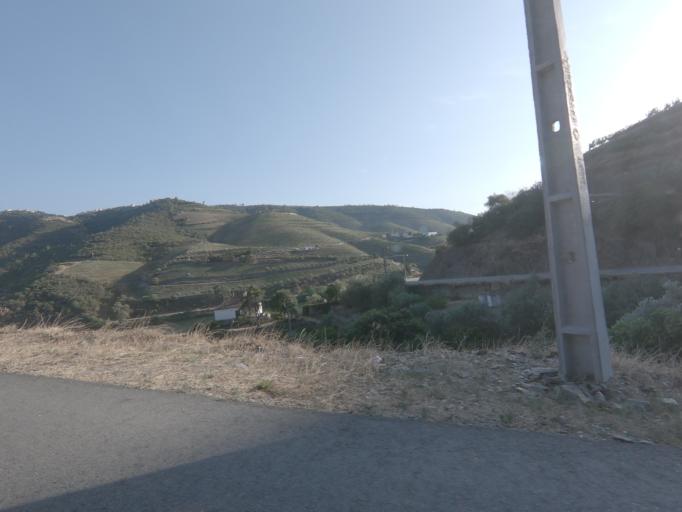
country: PT
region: Viseu
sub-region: Tabuaco
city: Tabuaco
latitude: 41.1623
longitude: -7.6084
